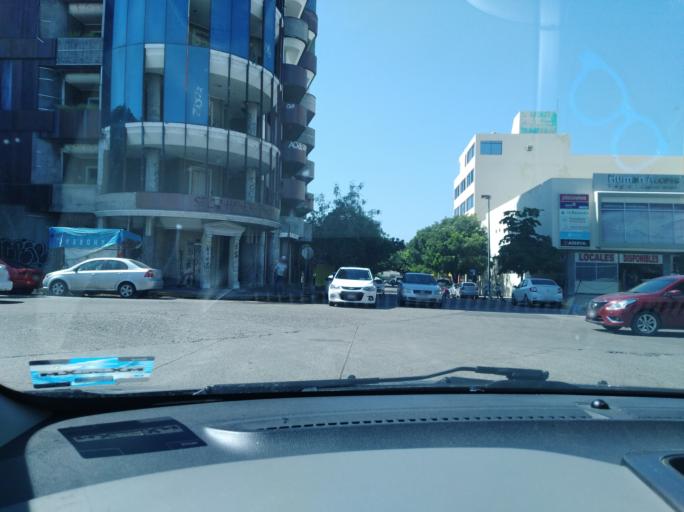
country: MX
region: Sinaloa
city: Culiacan
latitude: 24.7945
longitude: -107.4123
